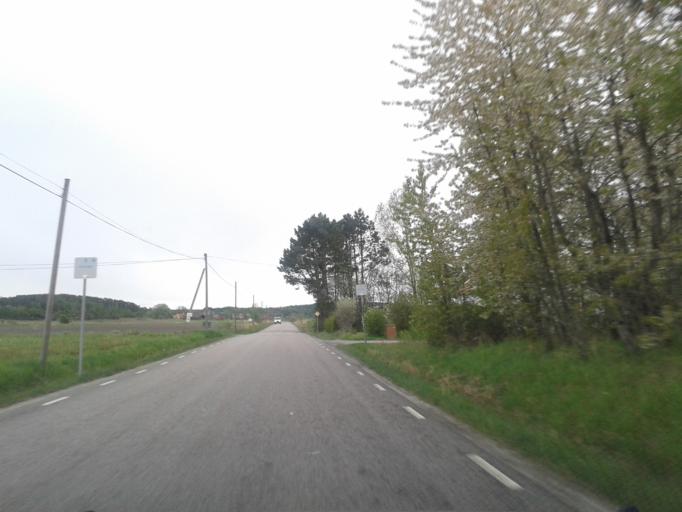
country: SE
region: Vaestra Goetaland
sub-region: Kungalvs Kommun
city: Kode
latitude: 57.9563
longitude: 11.8212
